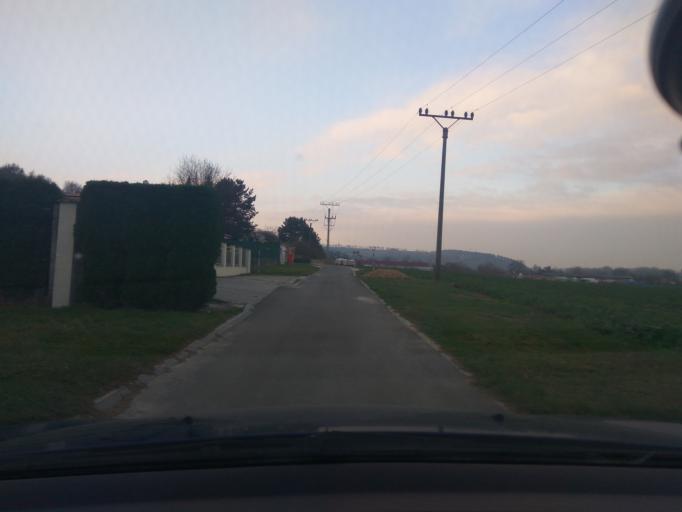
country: SK
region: Trnavsky
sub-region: Okres Trnava
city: Piestany
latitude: 48.5930
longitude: 17.8639
